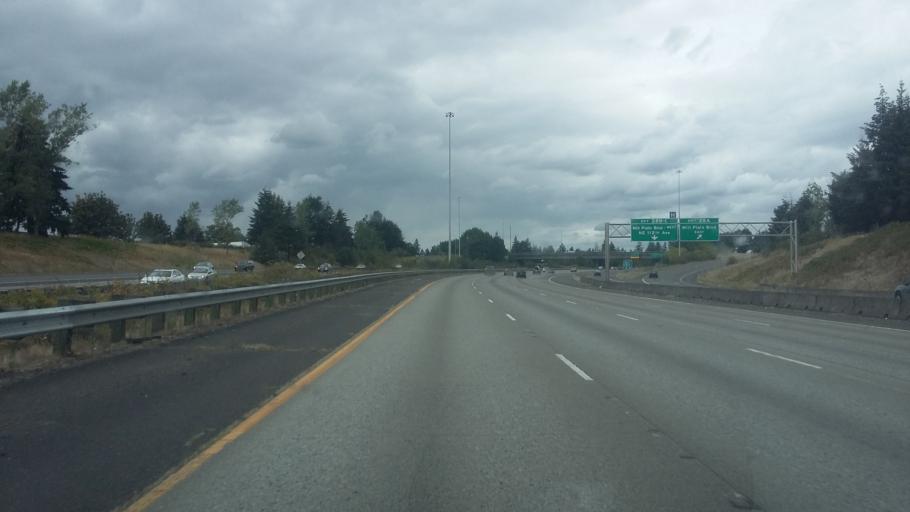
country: US
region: Washington
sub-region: Clark County
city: Orchards
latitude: 45.6171
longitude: -122.5567
